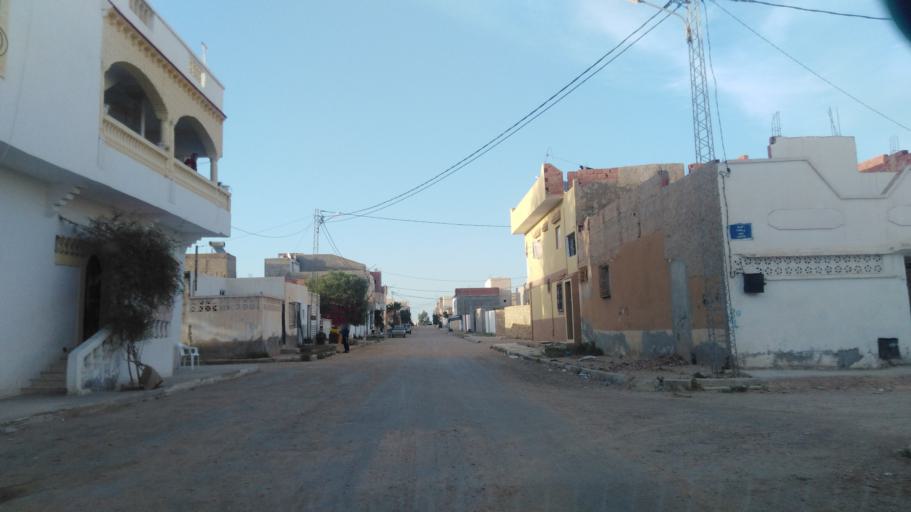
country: TN
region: Tataouine
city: Tataouine
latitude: 32.9404
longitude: 10.4569
